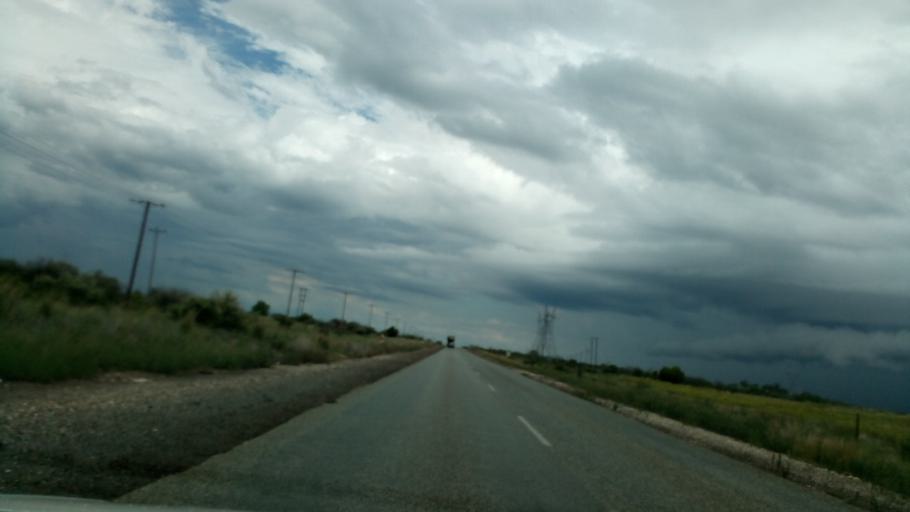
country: ZA
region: Northern Cape
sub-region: Siyanda District Municipality
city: Danielskuil
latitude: -28.2626
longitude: 24.0614
